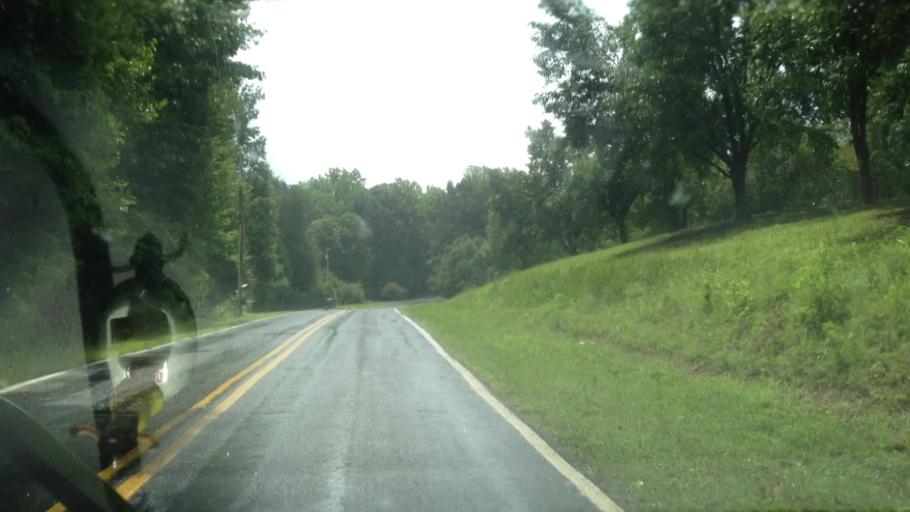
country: US
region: North Carolina
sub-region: Forsyth County
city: Walkertown
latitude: 36.2121
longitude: -80.1115
